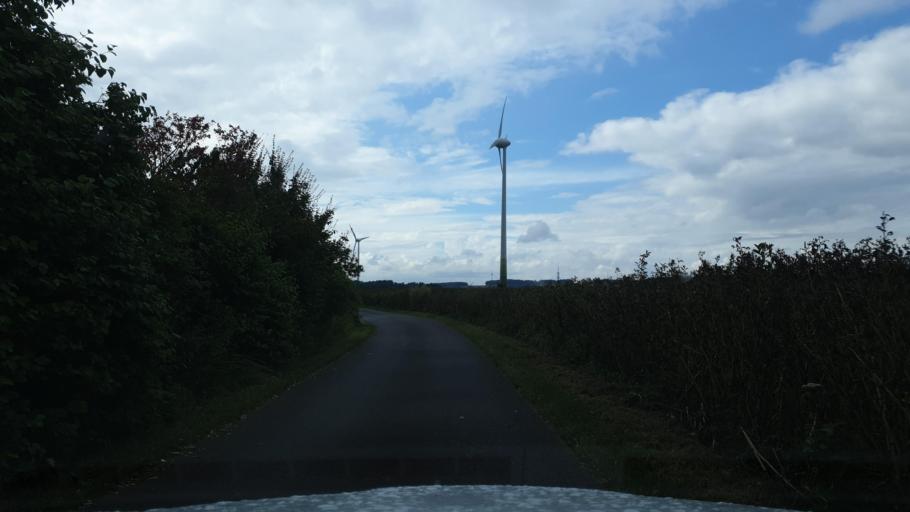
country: DE
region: North Rhine-Westphalia
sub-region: Regierungsbezirk Detmold
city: Bad Salzuflen
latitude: 52.1284
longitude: 8.7509
